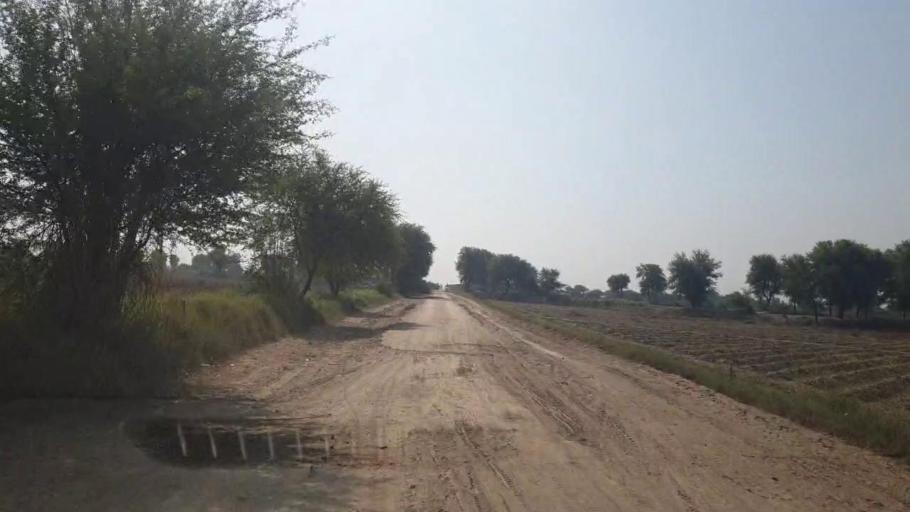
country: PK
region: Sindh
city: Shahdadpur
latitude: 25.9091
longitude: 68.7424
